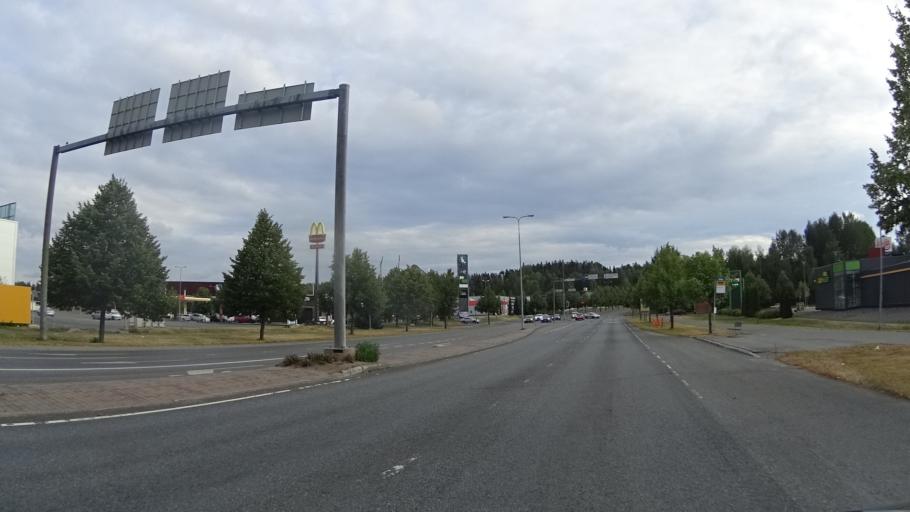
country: FI
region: Haeme
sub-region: Haemeenlinna
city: Haemeenlinna
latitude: 61.0092
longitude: 24.4167
